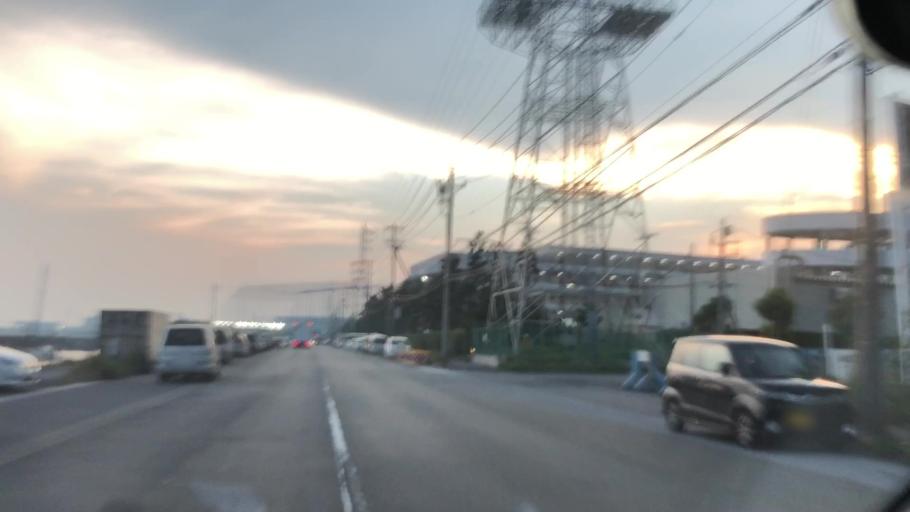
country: JP
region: Tokyo
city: Urayasu
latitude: 35.6673
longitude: 139.9363
